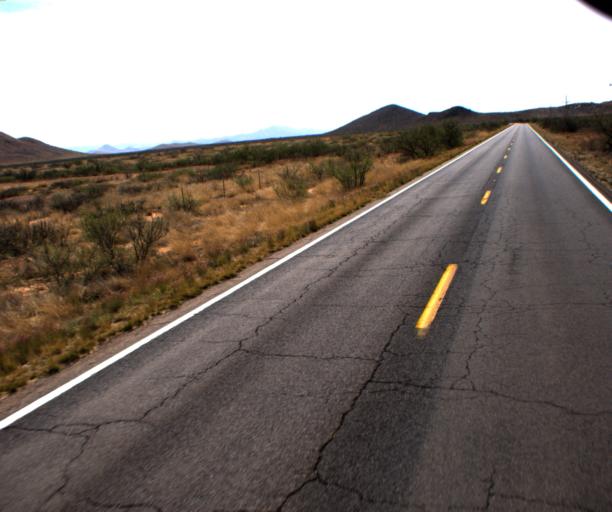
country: US
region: Arizona
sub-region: Cochise County
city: Tombstone
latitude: 31.9148
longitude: -109.8183
